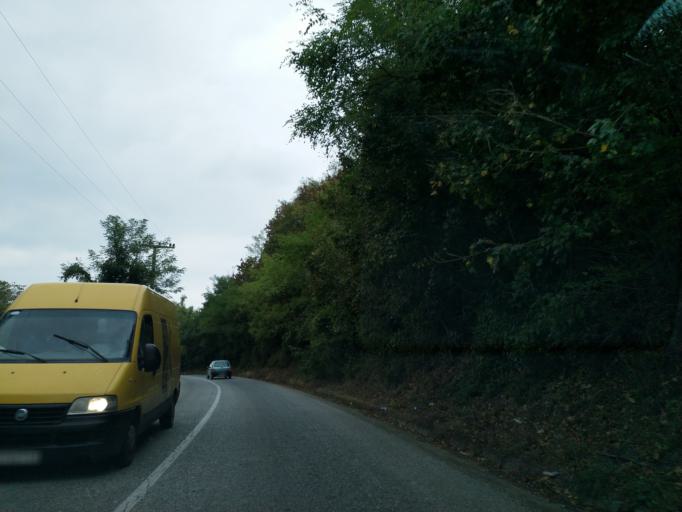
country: RS
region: Central Serbia
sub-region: Pomoravski Okrug
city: Jagodina
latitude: 44.0593
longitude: 21.1821
